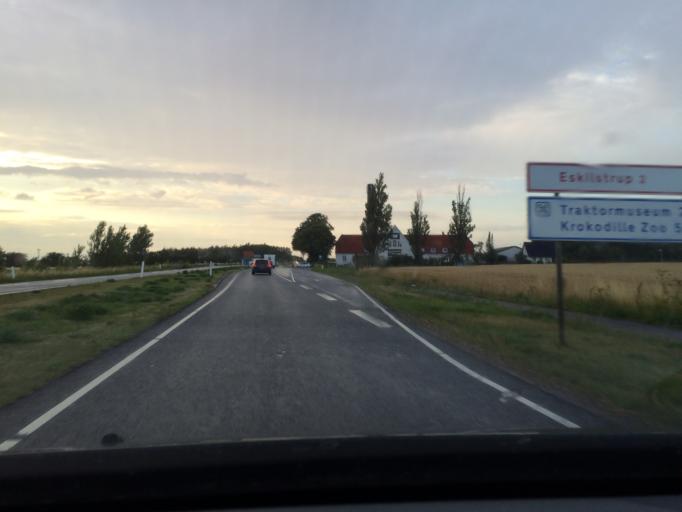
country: DK
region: Zealand
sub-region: Guldborgsund Kommune
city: Norre Alslev
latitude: 54.8532
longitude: 11.8565
